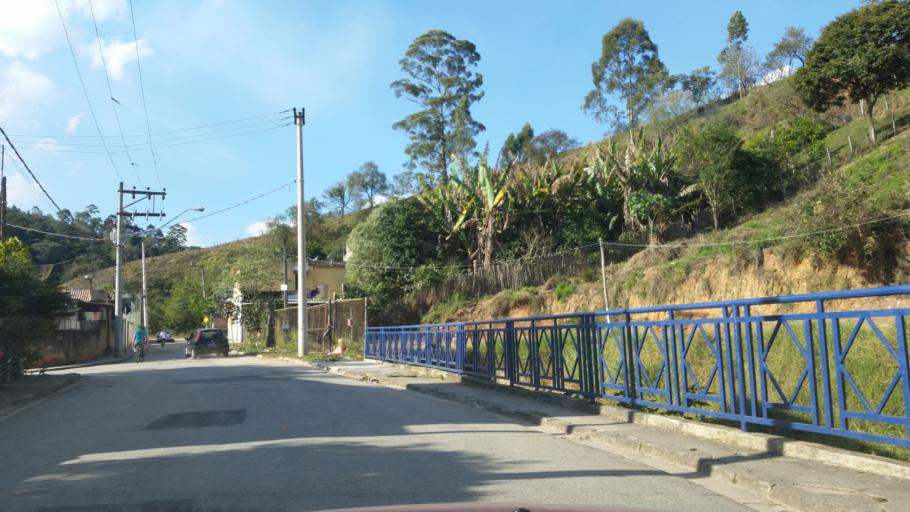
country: BR
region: Sao Paulo
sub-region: Mairinque
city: Mairinque
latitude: -23.5227
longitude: -47.2516
